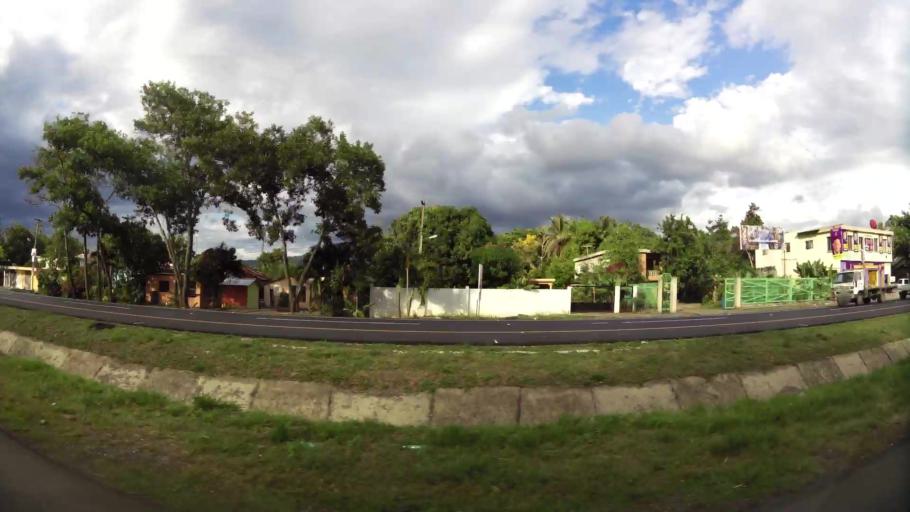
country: DO
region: Monsenor Nouel
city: Piedra Blanca
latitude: 18.8724
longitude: -70.3635
